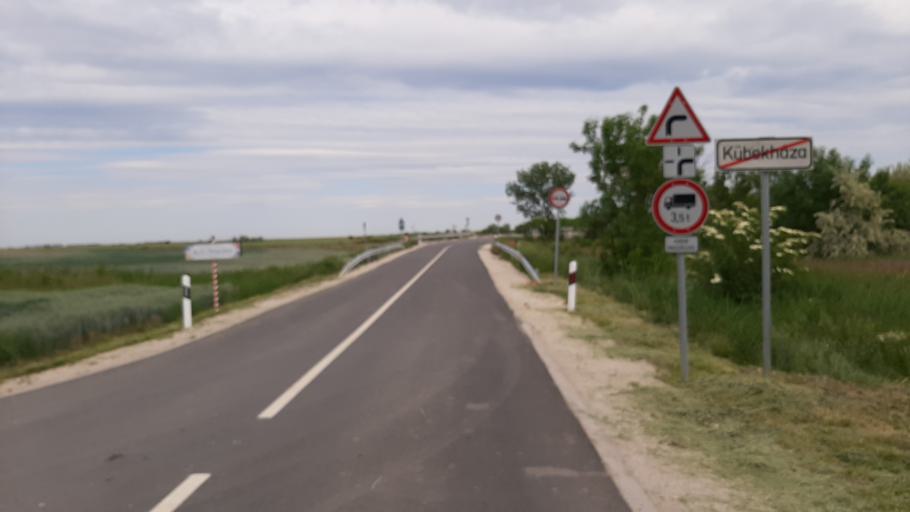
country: RO
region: Timis
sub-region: Comuna Beba Veche
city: Beba Veche
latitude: 46.1436
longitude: 20.2789
